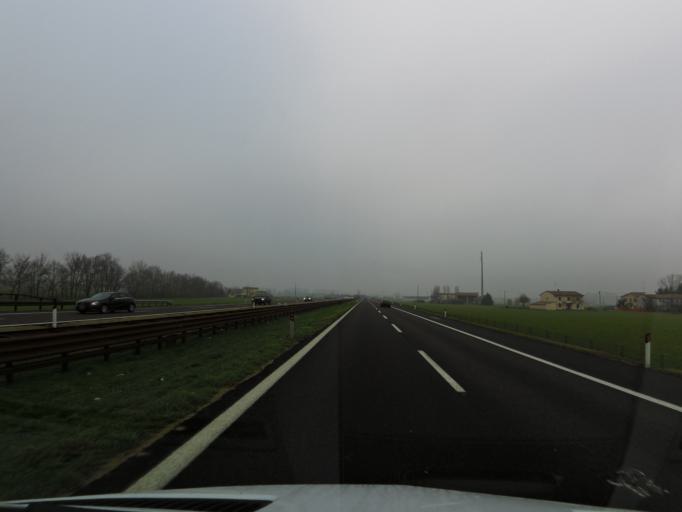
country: IT
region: Lombardy
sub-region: Provincia di Mantova
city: Pegognaga
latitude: 45.0360
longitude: 10.8539
